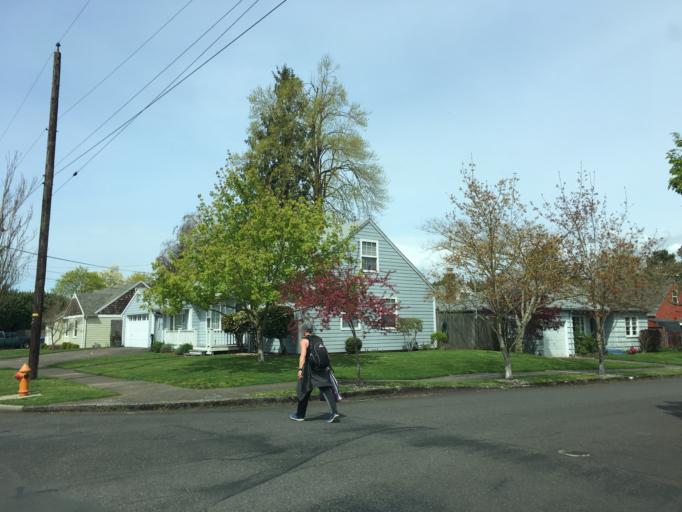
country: US
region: Oregon
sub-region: Multnomah County
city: Lents
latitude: 45.5443
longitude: -122.5732
